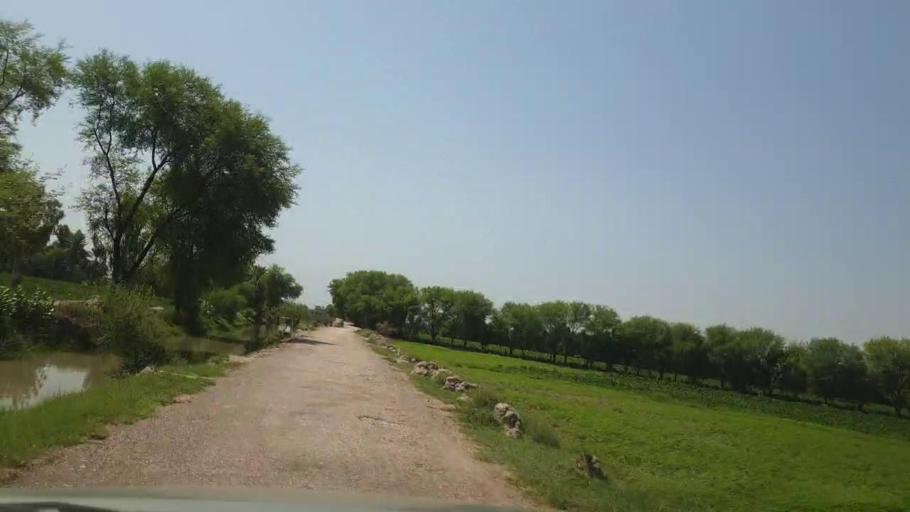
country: PK
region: Sindh
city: Rohri
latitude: 27.6546
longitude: 68.9829
